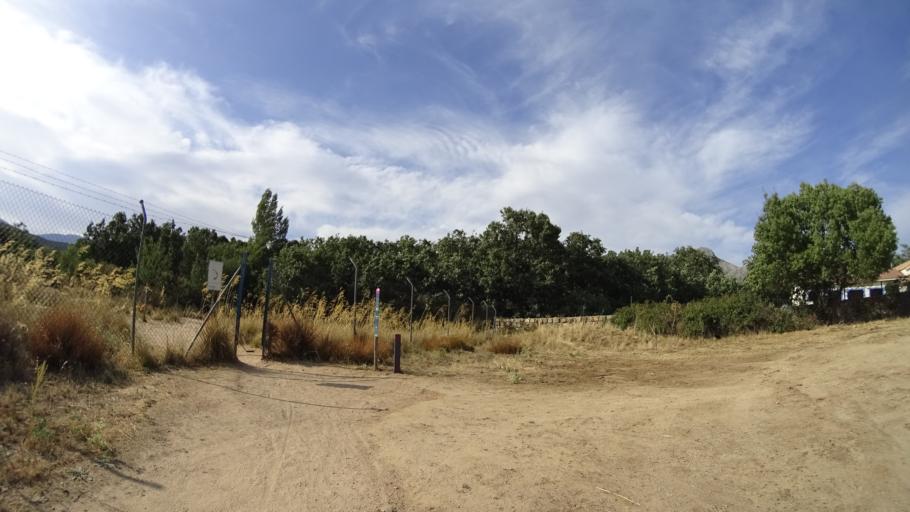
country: ES
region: Madrid
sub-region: Provincia de Madrid
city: Becerril de la Sierra
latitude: 40.7232
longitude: -4.0011
